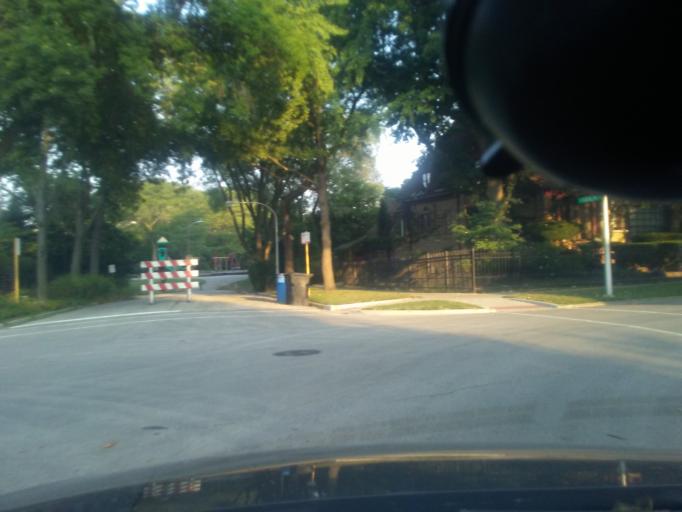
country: US
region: Illinois
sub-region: Cook County
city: Lincolnwood
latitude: 41.9812
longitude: -87.7045
